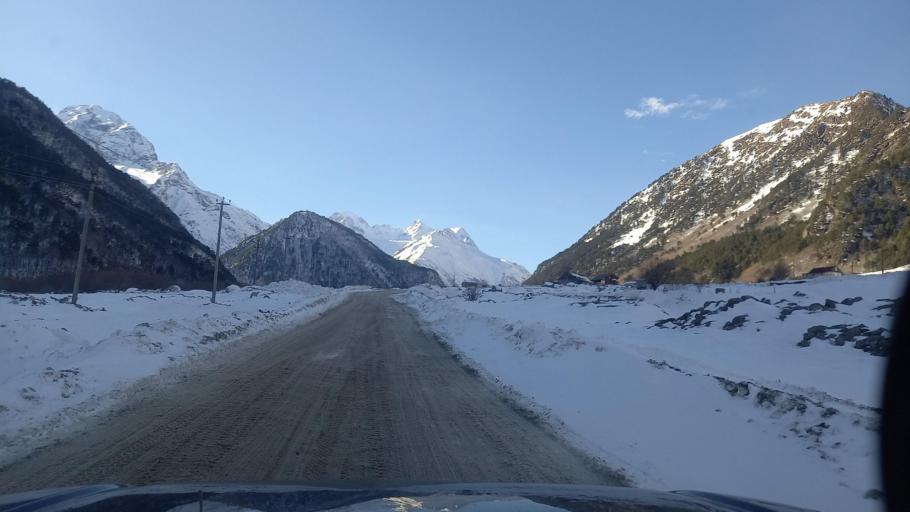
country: RU
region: Kabardino-Balkariya
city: Verkhnyaya Balkariya
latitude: 42.9014
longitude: 43.6315
